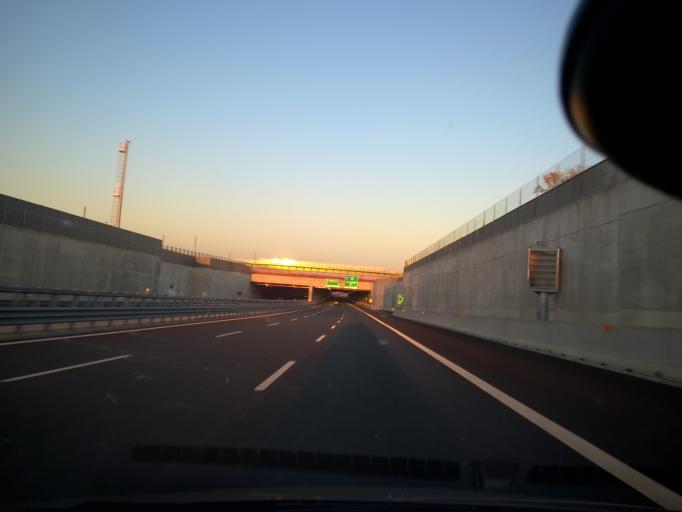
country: IT
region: Lombardy
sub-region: Provincia di Bergamo
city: Calvenzano
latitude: 45.5060
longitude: 9.6160
